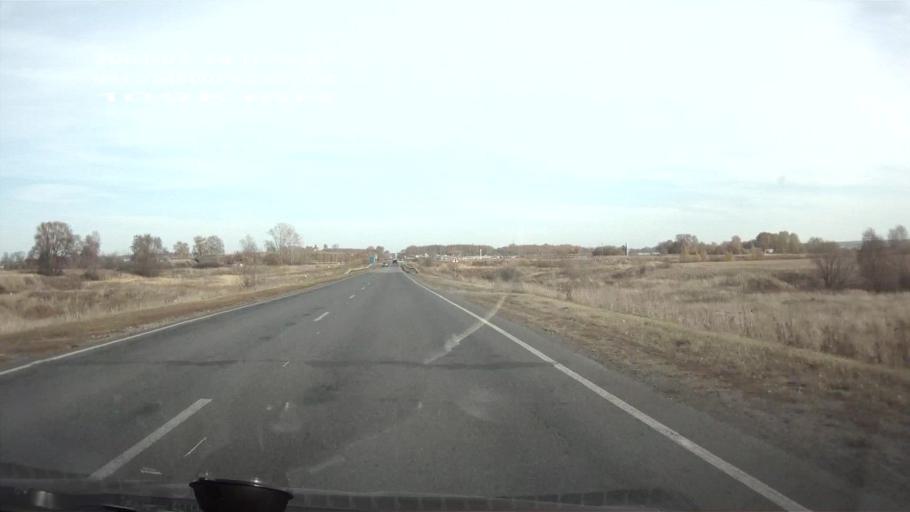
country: RU
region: Mordoviya
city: Atyashevo
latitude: 54.5546
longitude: 45.9642
